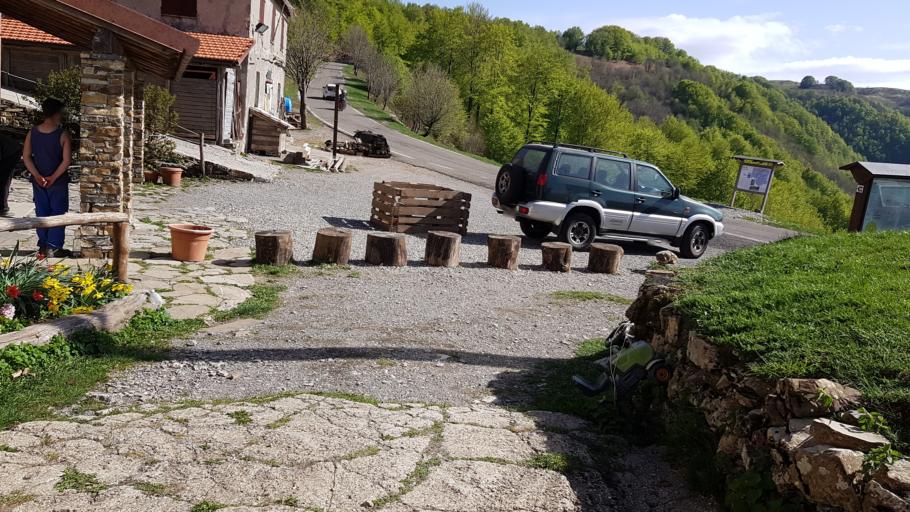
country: IT
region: Liguria
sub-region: Provincia di Genova
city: Fascia
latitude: 44.6019
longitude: 9.2049
